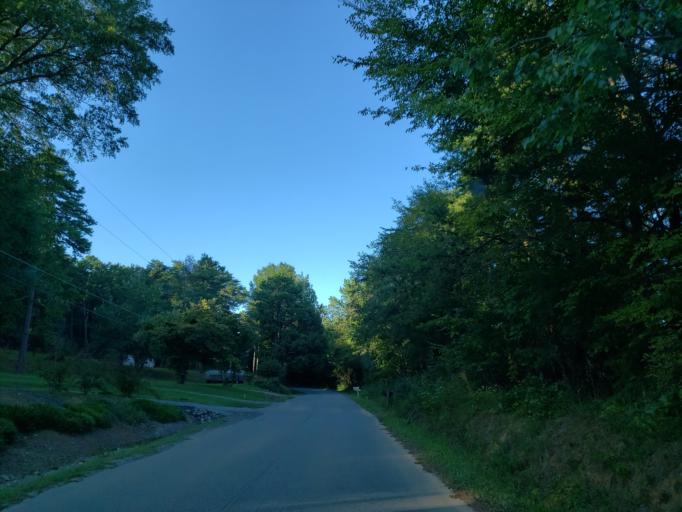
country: US
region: Georgia
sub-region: Bartow County
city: Rydal
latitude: 34.3039
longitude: -84.7327
